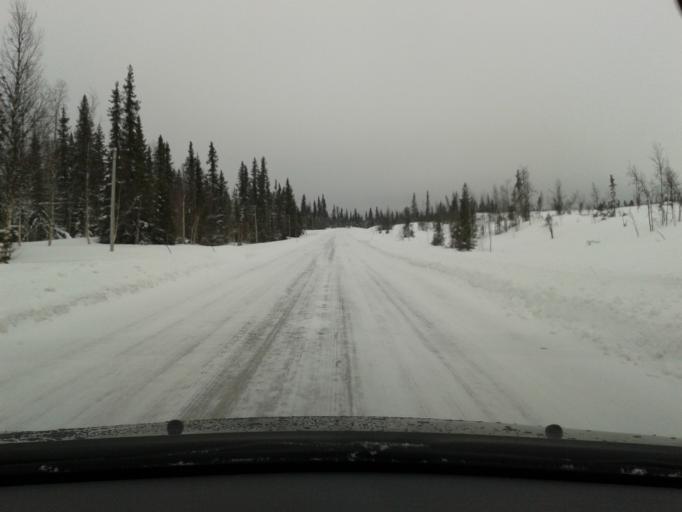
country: SE
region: Vaesterbotten
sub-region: Vilhelmina Kommun
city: Sjoberg
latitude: 65.1468
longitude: 15.8674
